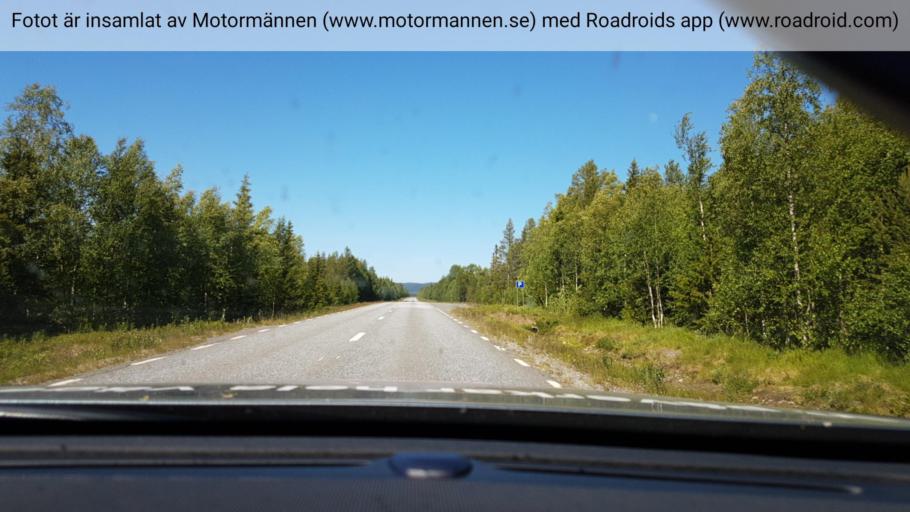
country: SE
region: Vaesterbotten
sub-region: Vilhelmina Kommun
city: Sjoberg
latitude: 64.8451
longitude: 15.9140
